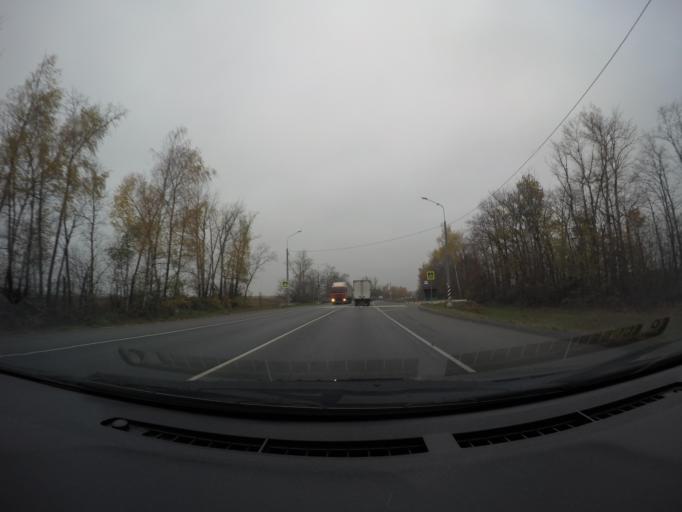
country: RU
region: Moskovskaya
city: Zhitnevo
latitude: 55.3624
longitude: 38.0013
